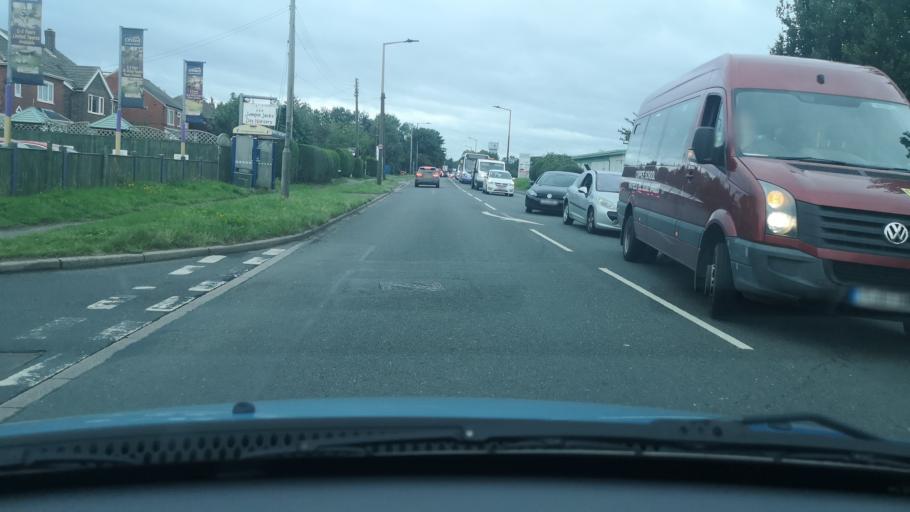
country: GB
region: England
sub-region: Doncaster
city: Kirk Sandall
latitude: 53.5567
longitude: -1.0777
